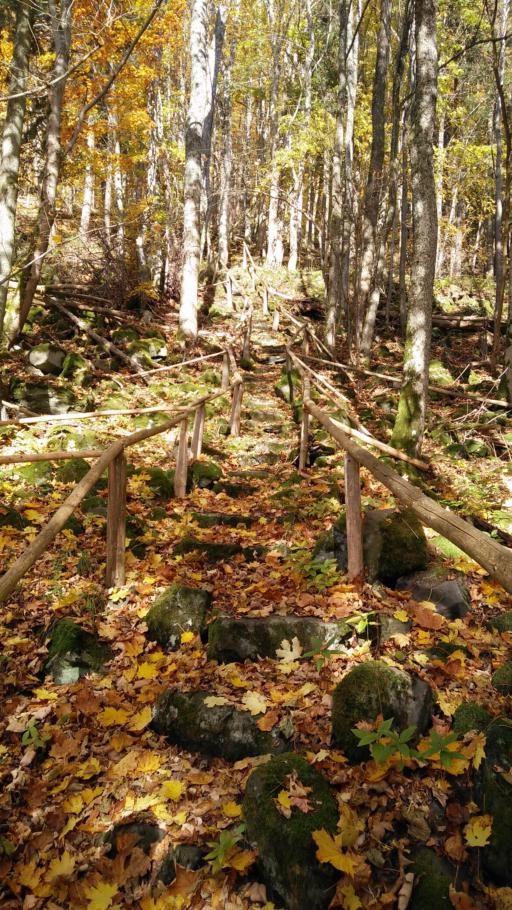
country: DE
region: Bavaria
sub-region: Regierungsbezirk Unterfranken
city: Oberelsbach
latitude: 50.4624
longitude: 10.0871
